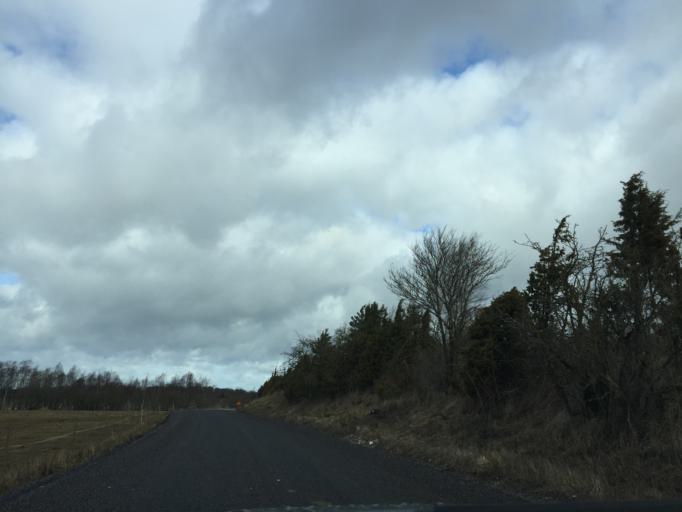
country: EE
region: Laeaene
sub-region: Haapsalu linn
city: Haapsalu
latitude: 58.6770
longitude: 23.5433
